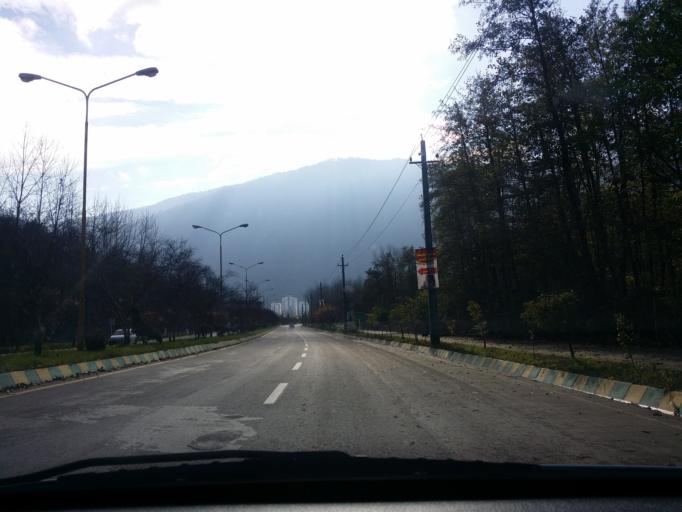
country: IR
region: Mazandaran
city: Chalus
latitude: 36.6815
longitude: 51.3054
